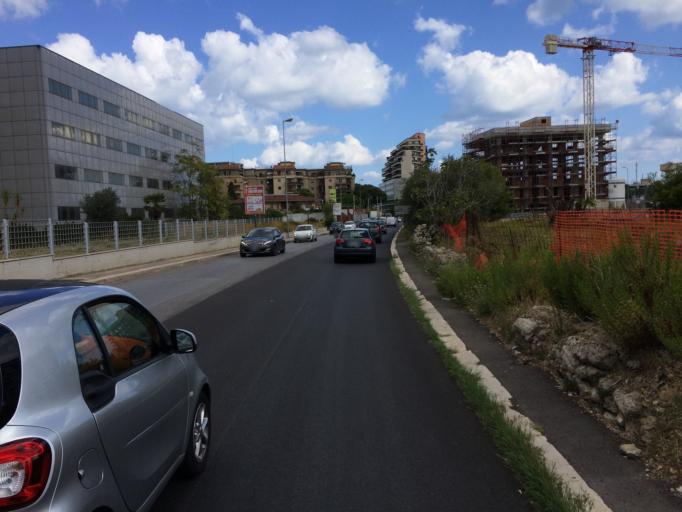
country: IT
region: Apulia
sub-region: Provincia di Bari
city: Bari
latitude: 41.1060
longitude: 16.8507
